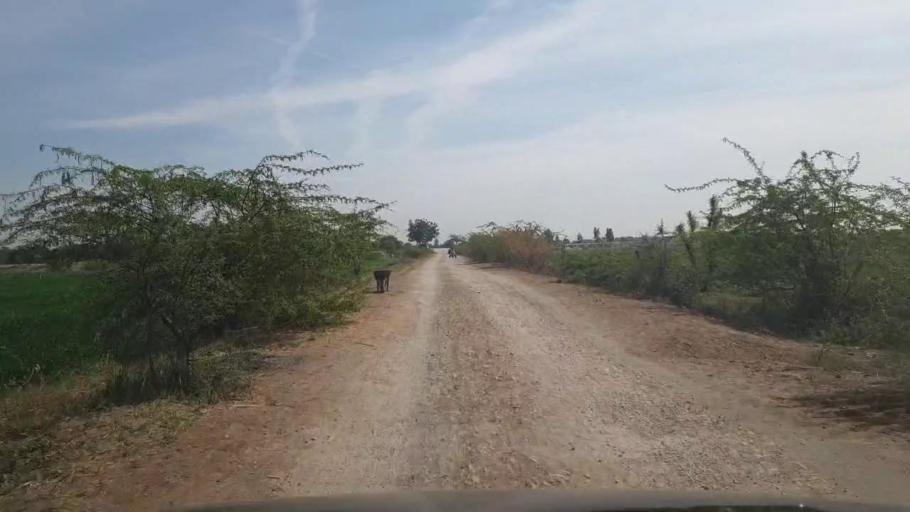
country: PK
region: Sindh
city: Umarkot
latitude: 25.3341
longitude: 69.6017
